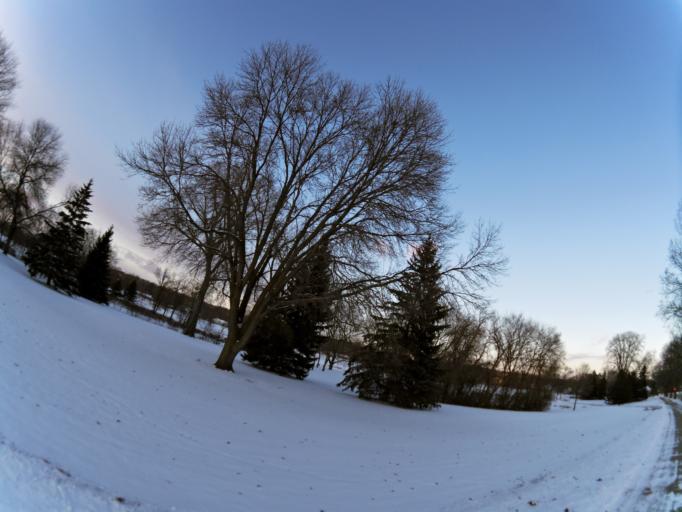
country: US
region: Minnesota
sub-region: Olmsted County
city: Rochester
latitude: 44.0302
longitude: -92.4534
